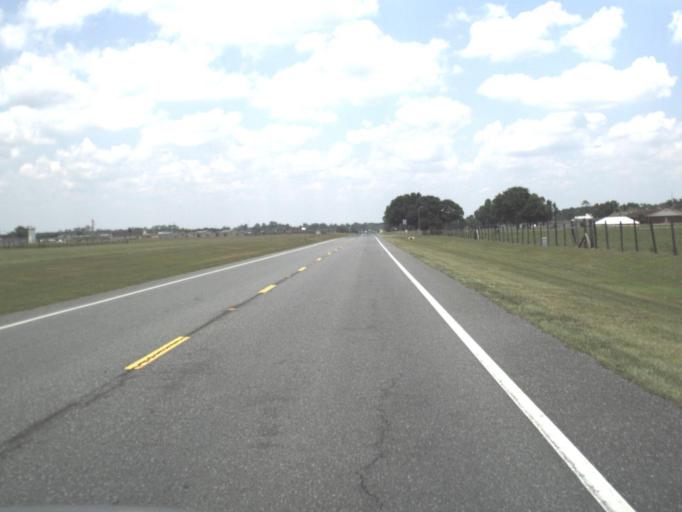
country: US
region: Florida
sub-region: Bradford County
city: Starke
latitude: 30.0566
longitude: -82.1770
